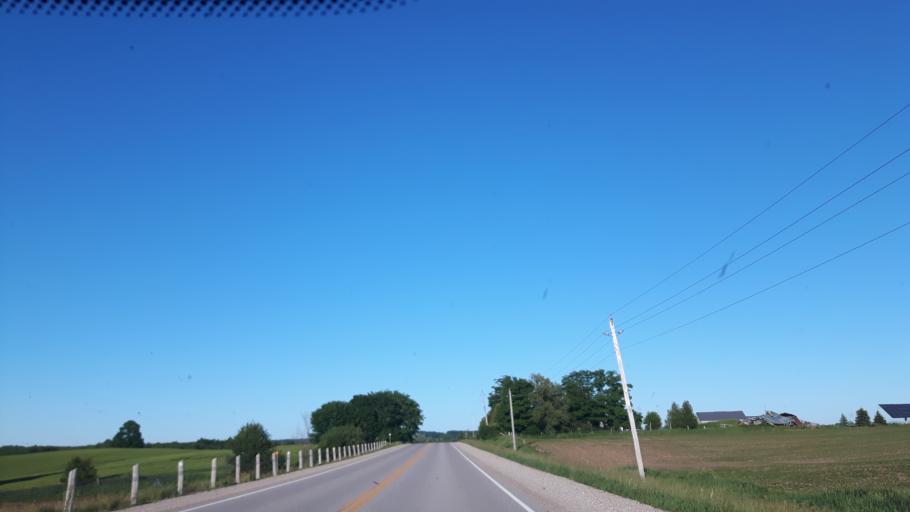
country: CA
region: Ontario
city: Goderich
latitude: 43.6428
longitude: -81.6167
